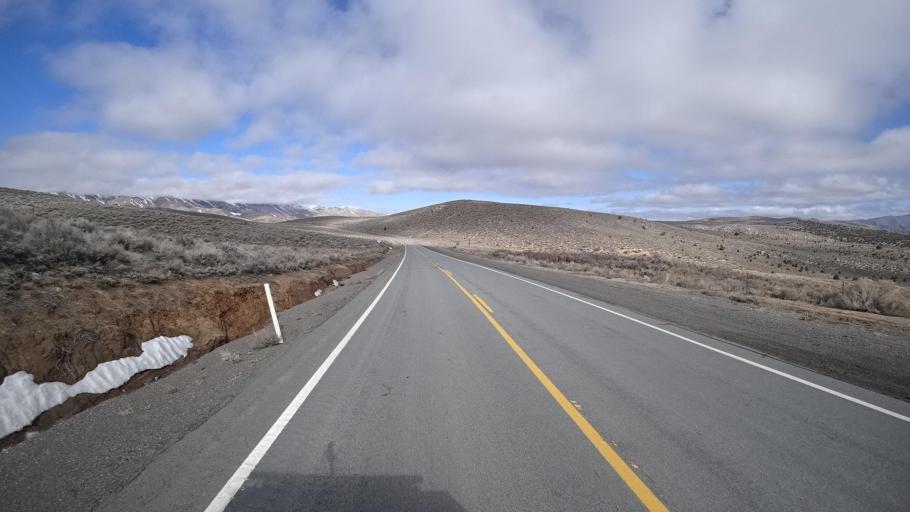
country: US
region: Nevada
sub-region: Washoe County
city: Cold Springs
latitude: 39.7985
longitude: -119.9015
